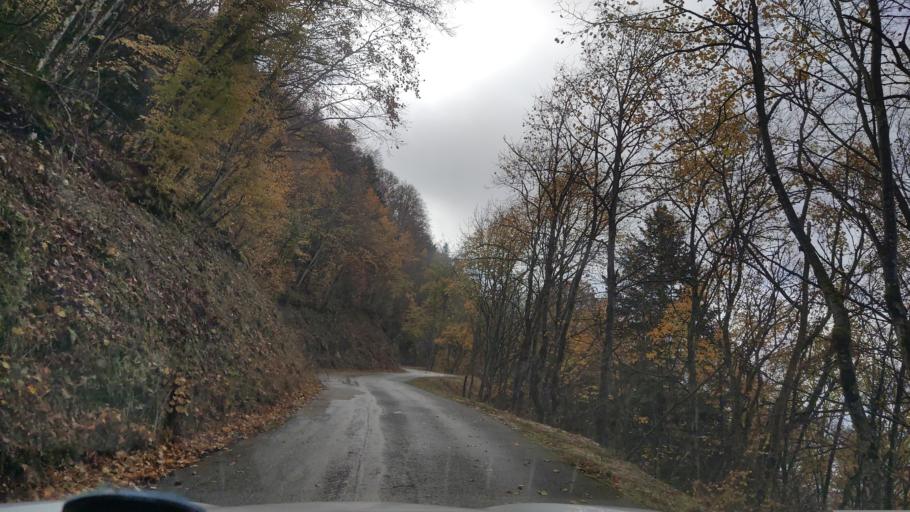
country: FR
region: Rhone-Alpes
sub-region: Departement de la Savoie
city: Le Bourget-du-Lac
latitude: 45.6550
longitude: 5.8053
